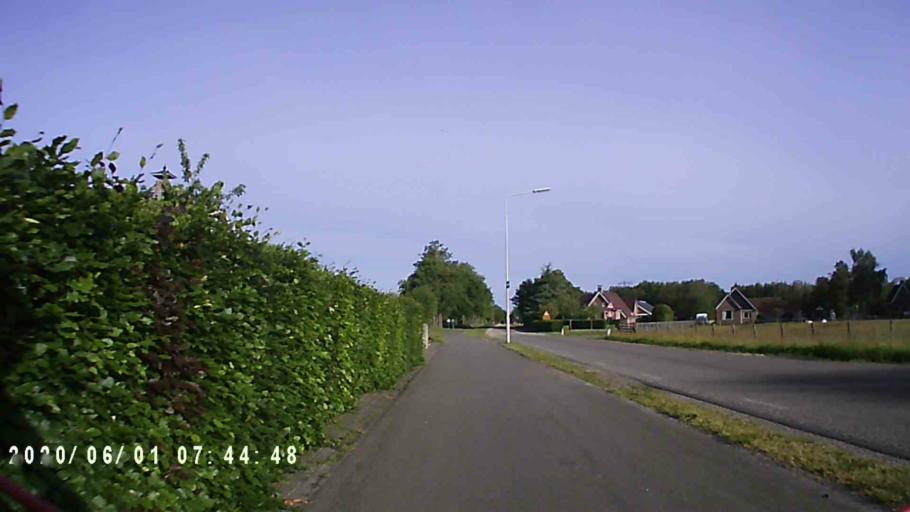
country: NL
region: Friesland
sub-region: Gemeente Dantumadiel
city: Rinsumageast
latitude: 53.2919
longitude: 5.9657
